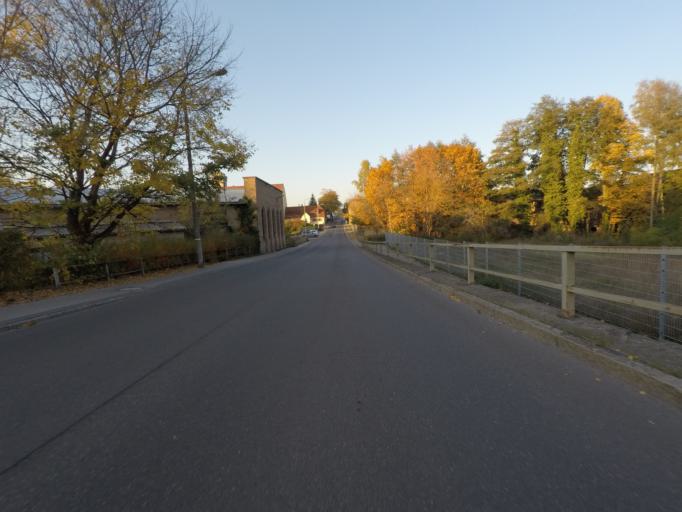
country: DE
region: Brandenburg
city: Melchow
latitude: 52.8442
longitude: 13.7254
